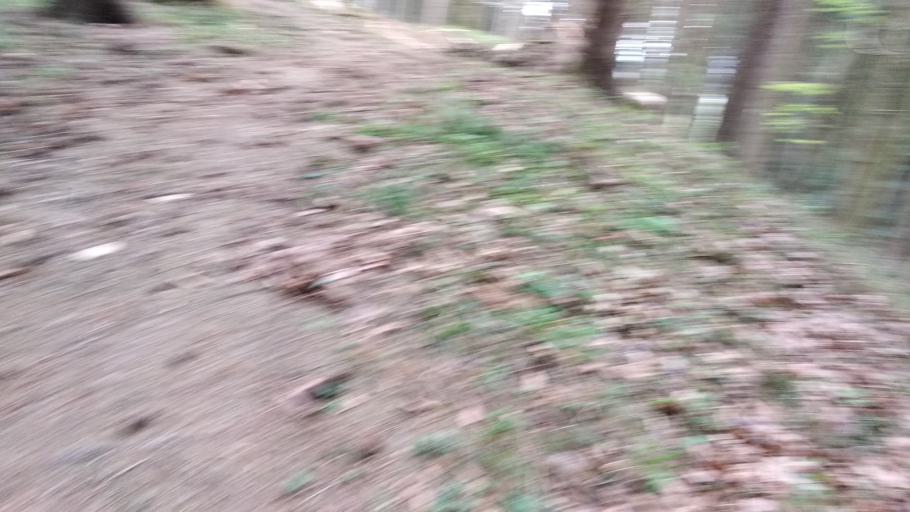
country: DE
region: Bavaria
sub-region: Swabia
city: Kronburg
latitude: 47.8902
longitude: 10.1766
